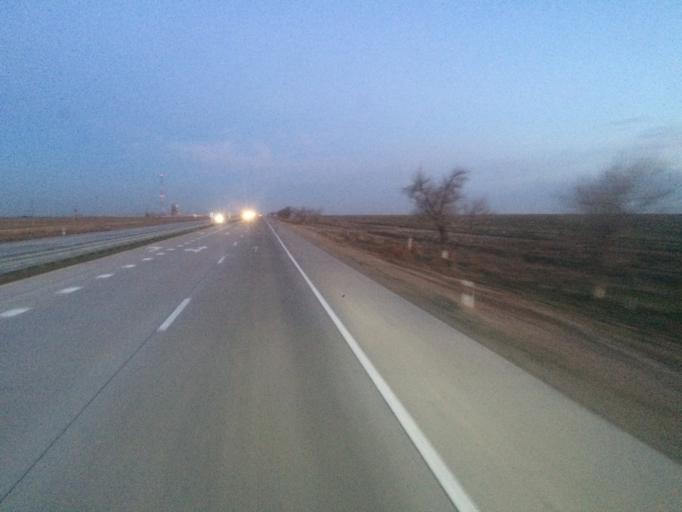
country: KZ
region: Ongtustik Qazaqstan
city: Temirlanovka
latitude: 42.8346
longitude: 69.1189
